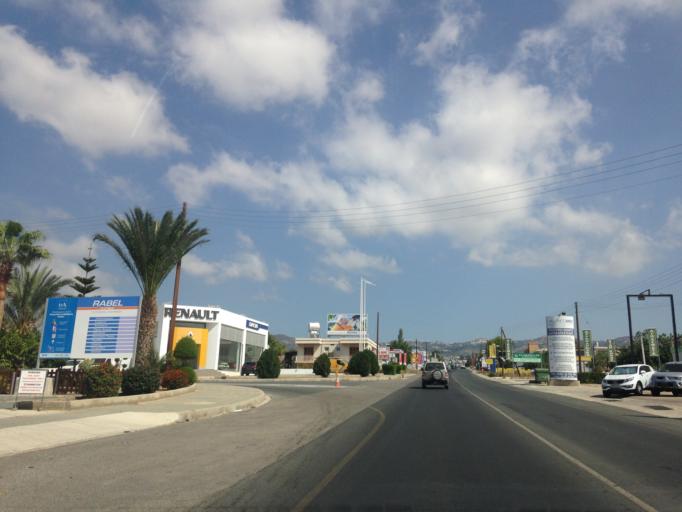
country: CY
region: Pafos
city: Empa
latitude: 34.7977
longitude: 32.4401
